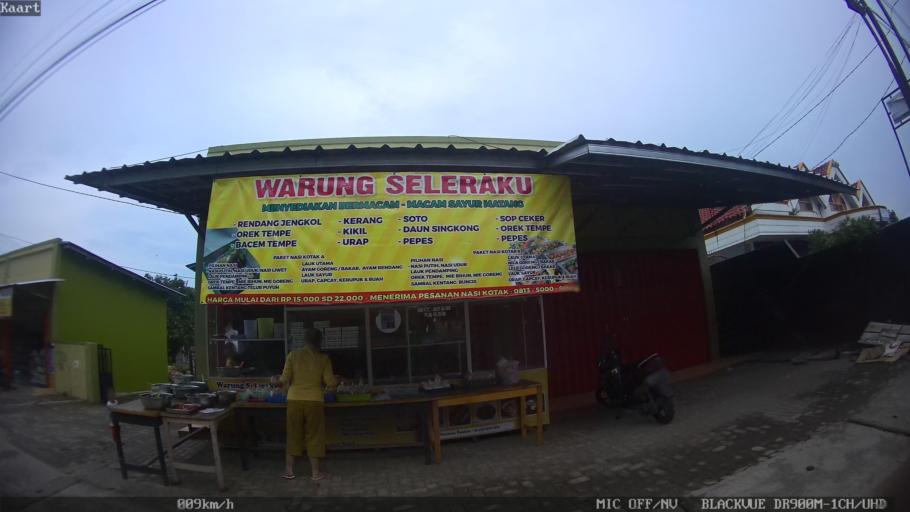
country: ID
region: Lampung
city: Kedaton
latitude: -5.3999
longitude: 105.2308
